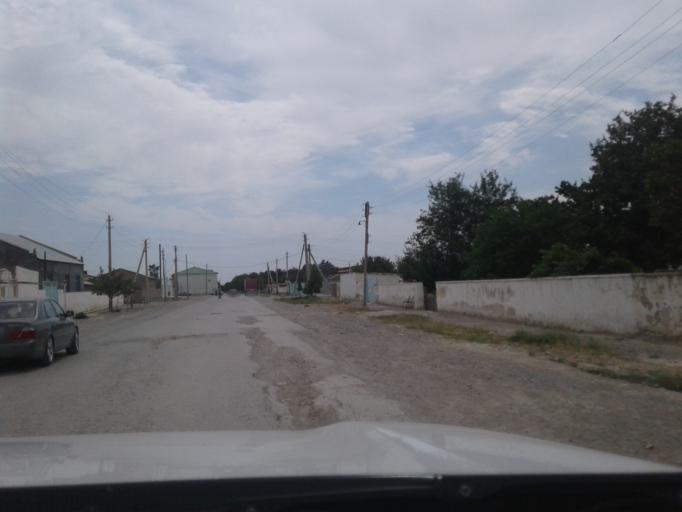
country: TM
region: Balkan
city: Serdar
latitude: 38.9883
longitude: 56.2798
